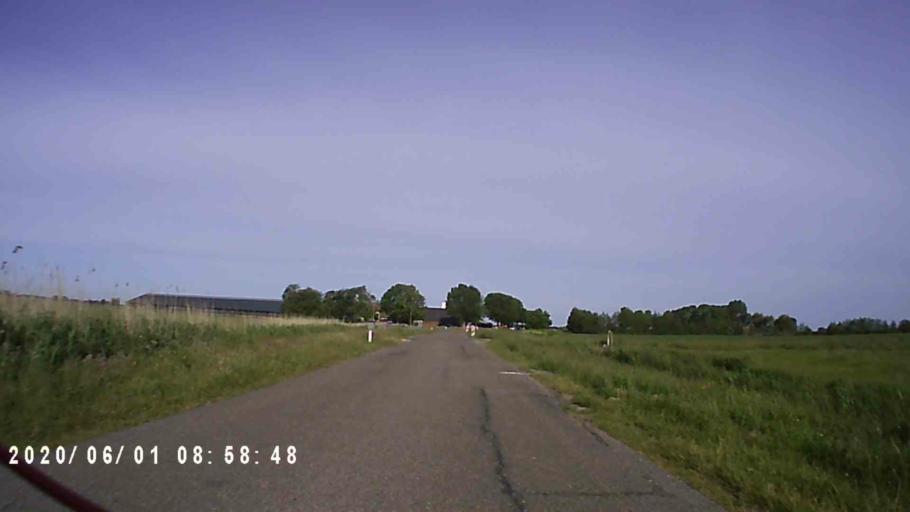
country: NL
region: Friesland
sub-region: Gemeente Ferwerderadiel
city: Hallum
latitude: 53.2820
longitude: 5.8029
